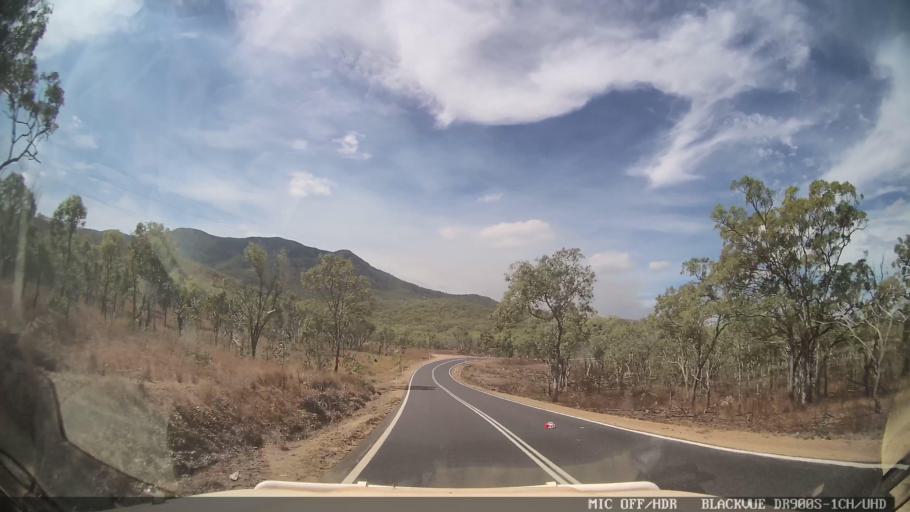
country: AU
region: Queensland
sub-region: Cairns
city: Port Douglas
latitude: -16.6693
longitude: 145.2635
